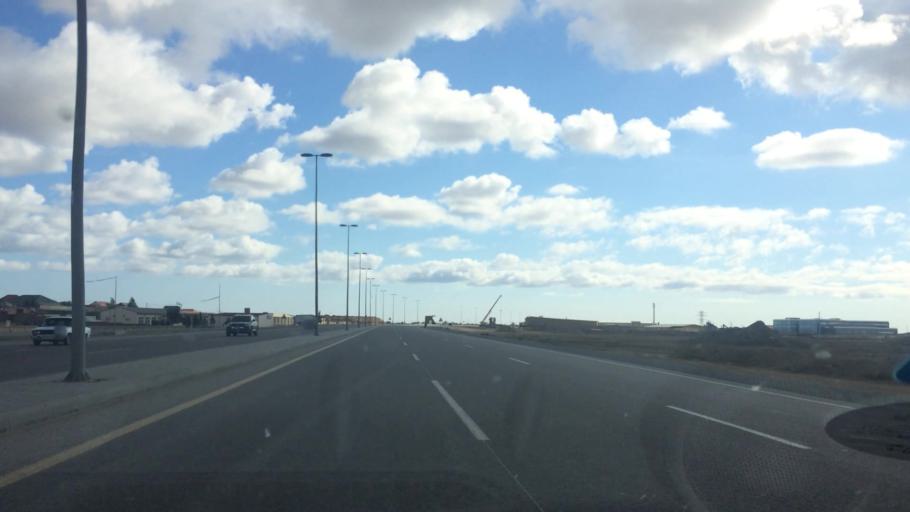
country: AZ
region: Baki
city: Qala
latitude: 40.4567
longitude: 50.1366
